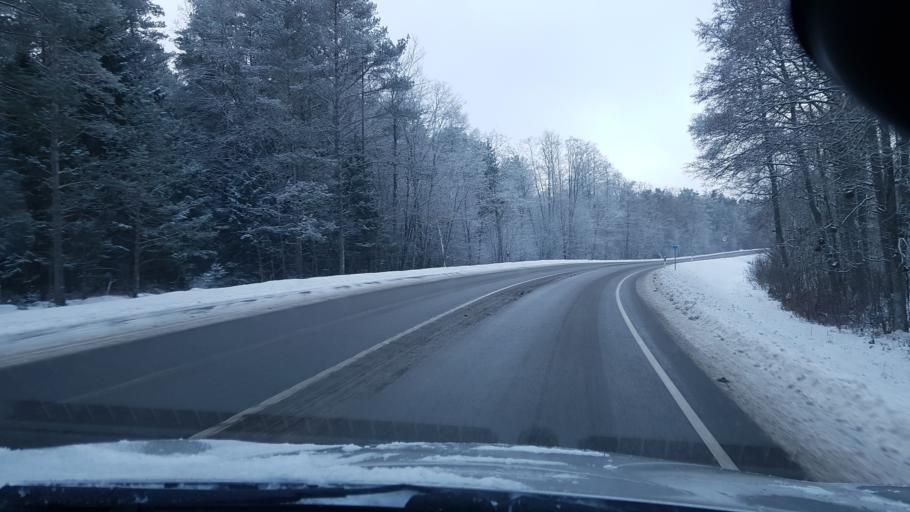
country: EE
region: Harju
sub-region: Keila linn
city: Keila
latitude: 59.3377
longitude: 24.2512
